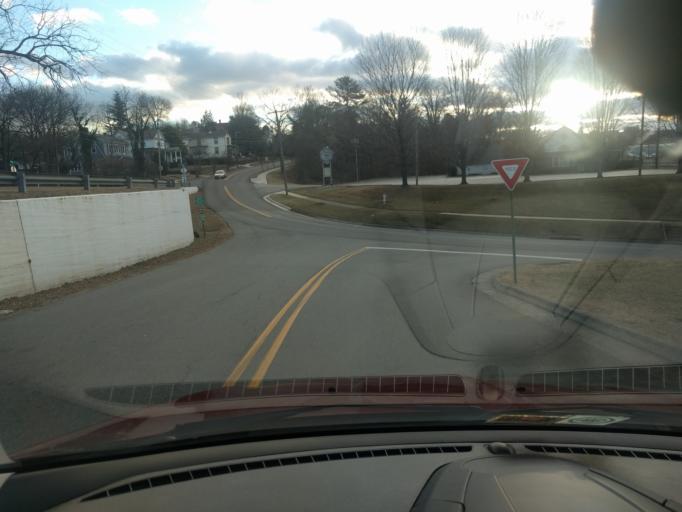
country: US
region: Virginia
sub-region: City of Bedford
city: Bedford
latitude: 37.3376
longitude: -79.5289
